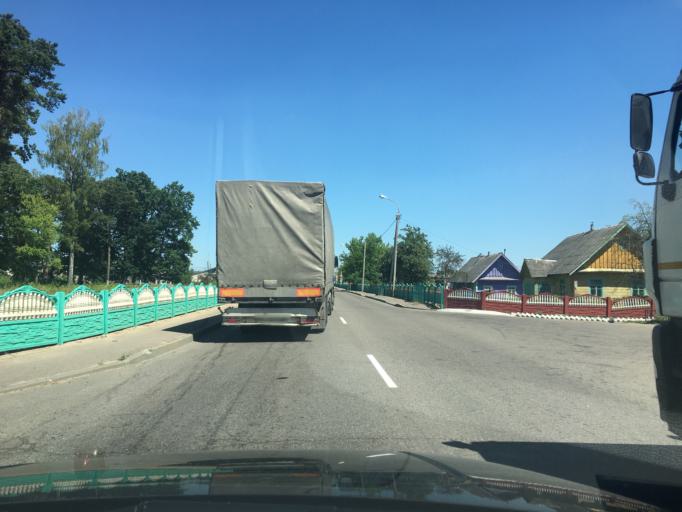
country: BY
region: Grodnenskaya
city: Iwye
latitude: 54.0290
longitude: 25.9252
